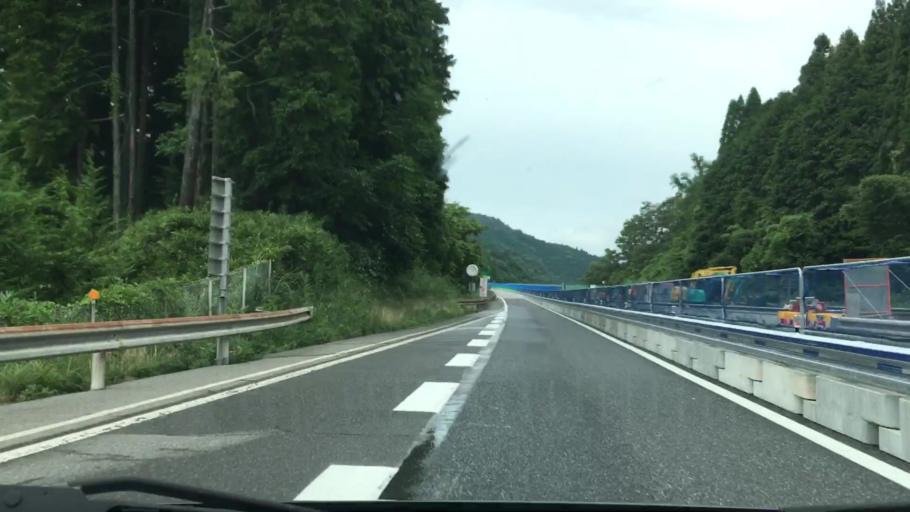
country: JP
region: Okayama
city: Niimi
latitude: 35.0278
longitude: 133.5779
